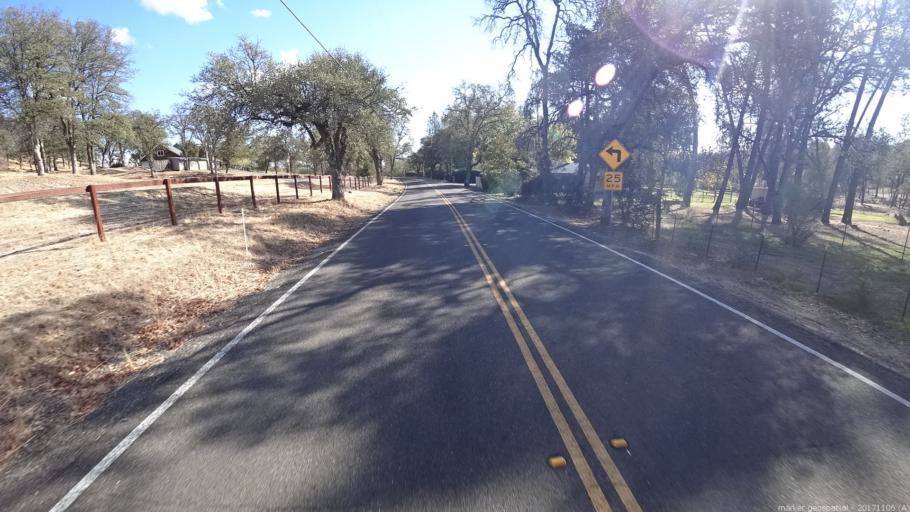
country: US
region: California
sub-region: Shasta County
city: Palo Cedro
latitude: 40.5920
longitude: -122.2482
